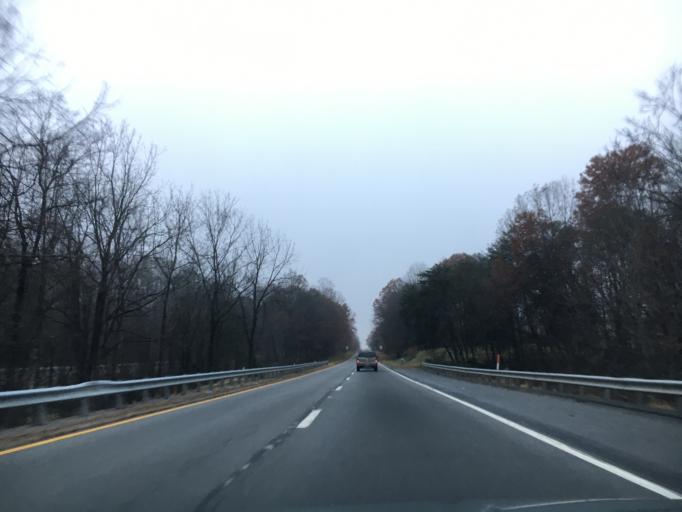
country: US
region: Virginia
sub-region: Prince Edward County
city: Hampden Sydney
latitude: 37.3019
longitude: -78.5698
